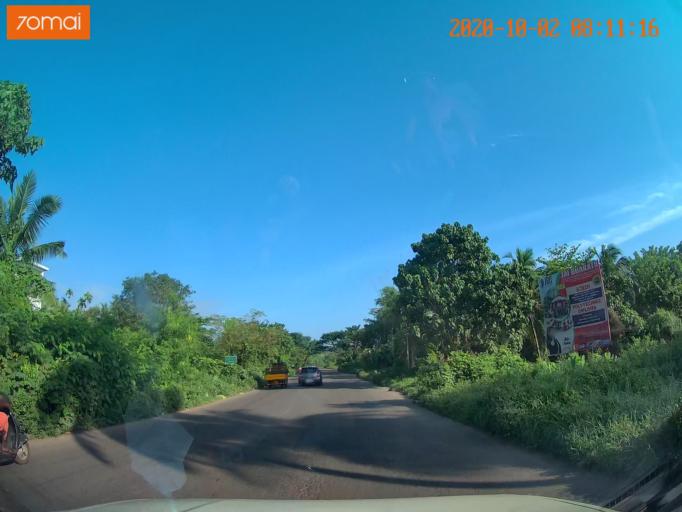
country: IN
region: Kerala
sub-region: Kozhikode
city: Kozhikode
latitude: 11.2732
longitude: 75.8083
